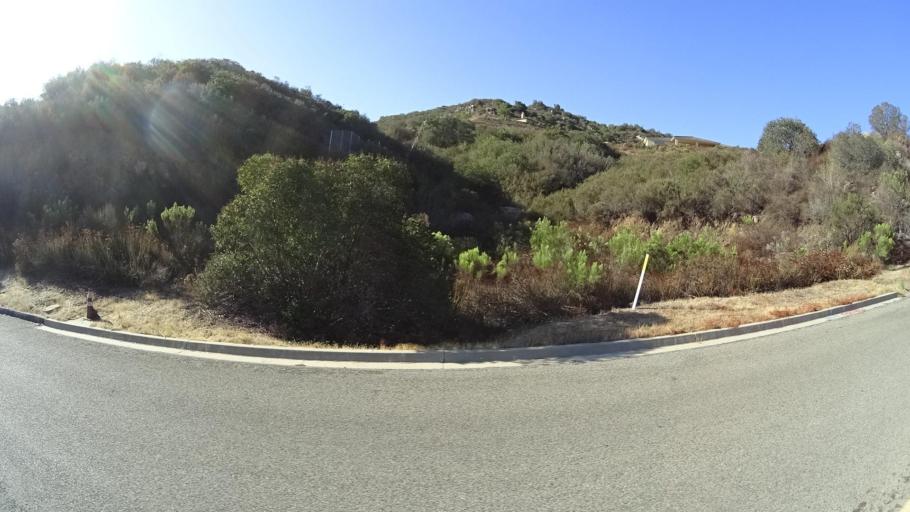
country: US
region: California
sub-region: San Diego County
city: Lakeside
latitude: 32.8998
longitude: -116.8945
